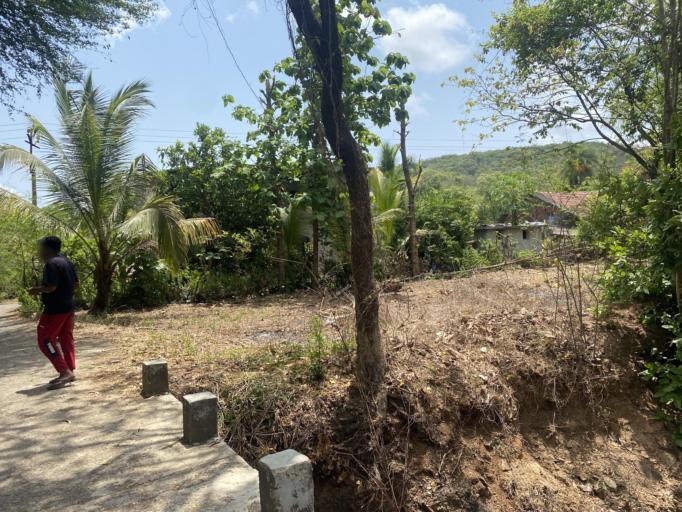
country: IN
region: Gujarat
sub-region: Valsad
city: Vapi
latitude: 20.3177
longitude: 72.8365
